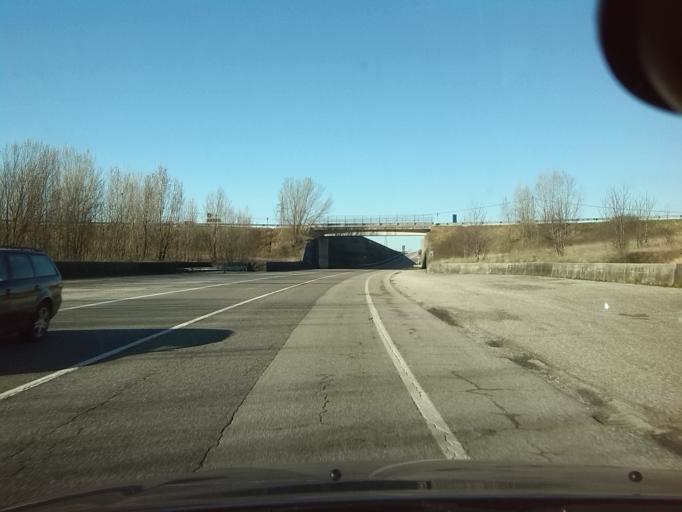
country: IT
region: Friuli Venezia Giulia
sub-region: Provincia di Udine
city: Cividale del Friuli
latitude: 46.0865
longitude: 13.4047
